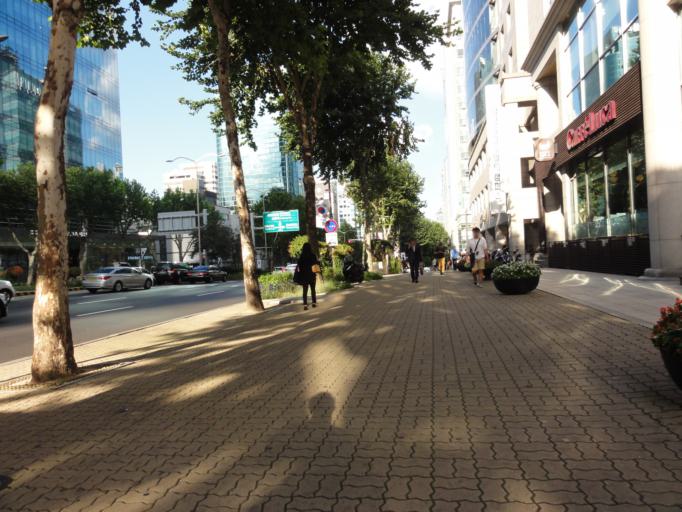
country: KR
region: Seoul
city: Seoul
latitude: 37.5016
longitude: 127.0387
